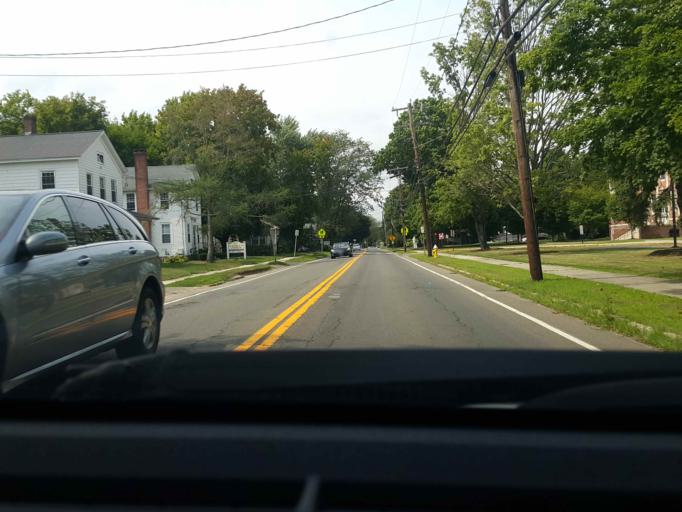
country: US
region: Connecticut
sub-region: New Haven County
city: Guilford
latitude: 41.2916
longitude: -72.6855
